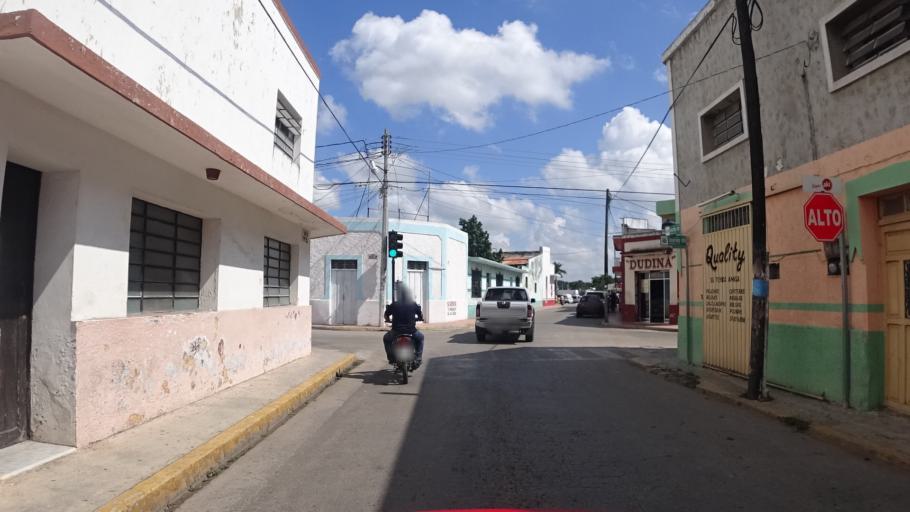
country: MX
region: Yucatan
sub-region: Tizimin
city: Tizimin
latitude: 21.1417
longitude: -88.1526
